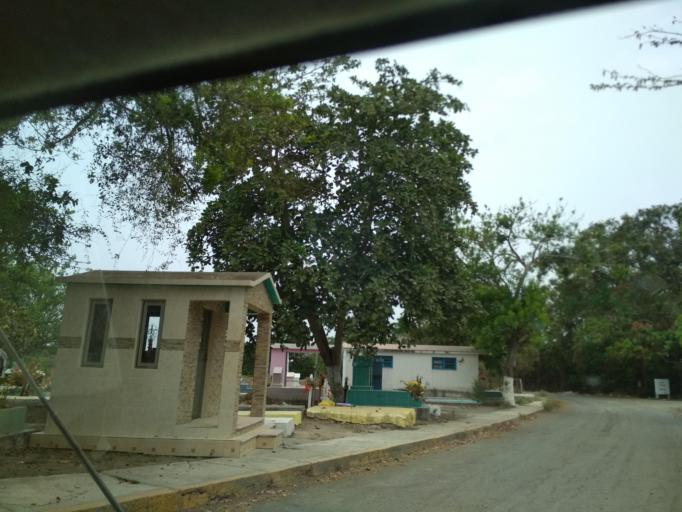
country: MX
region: Veracruz
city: Paso del Toro
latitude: 19.0438
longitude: -96.1480
